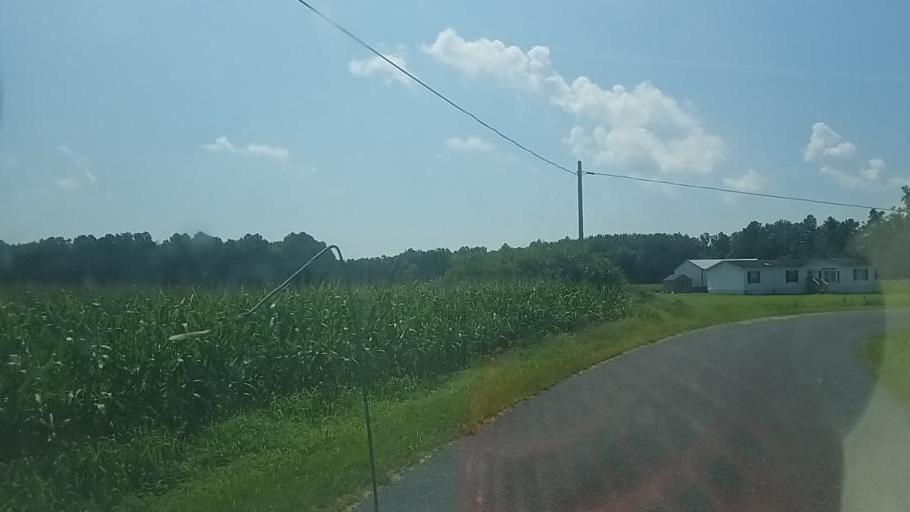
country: US
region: Maryland
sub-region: Worcester County
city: Berlin
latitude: 38.2908
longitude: -75.2957
